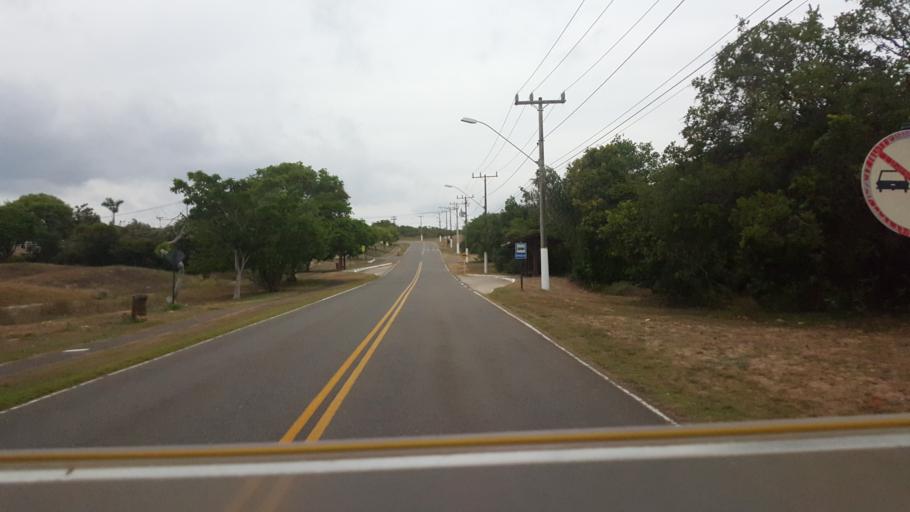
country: BR
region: Bahia
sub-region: Mata De Sao Joao
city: Mata de Sao Joao
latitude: -12.4260
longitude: -37.9225
